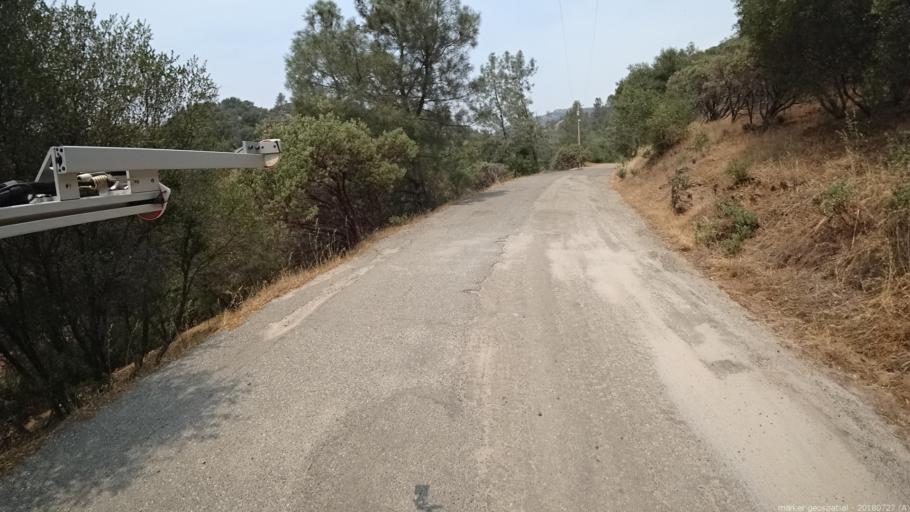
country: US
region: California
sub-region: Madera County
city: Coarsegold
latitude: 37.2719
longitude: -119.6894
